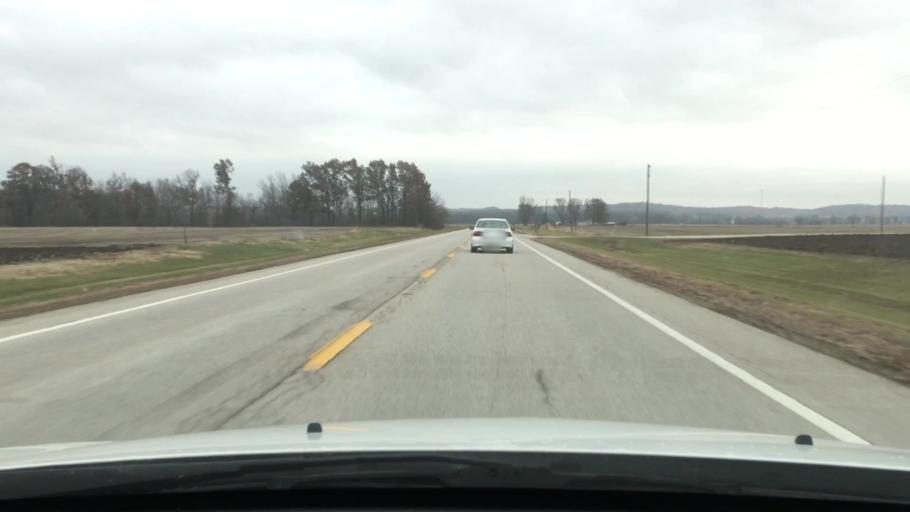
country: US
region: Missouri
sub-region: Pike County
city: Louisiana
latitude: 39.4914
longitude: -91.0076
